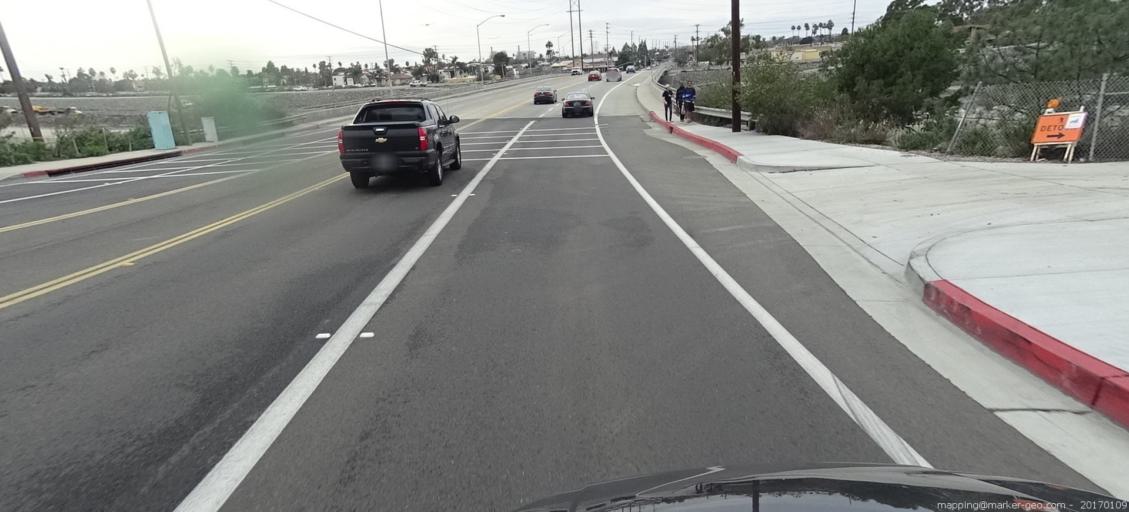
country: US
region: California
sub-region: Orange County
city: Costa Mesa
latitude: 33.6509
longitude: -117.9497
